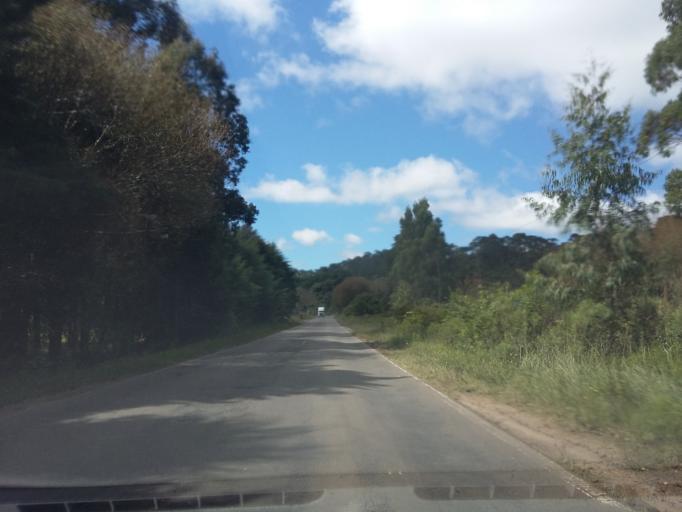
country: BR
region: Santa Catarina
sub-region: Sao Joaquim
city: Sao Joaquim
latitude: -28.2317
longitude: -49.8446
